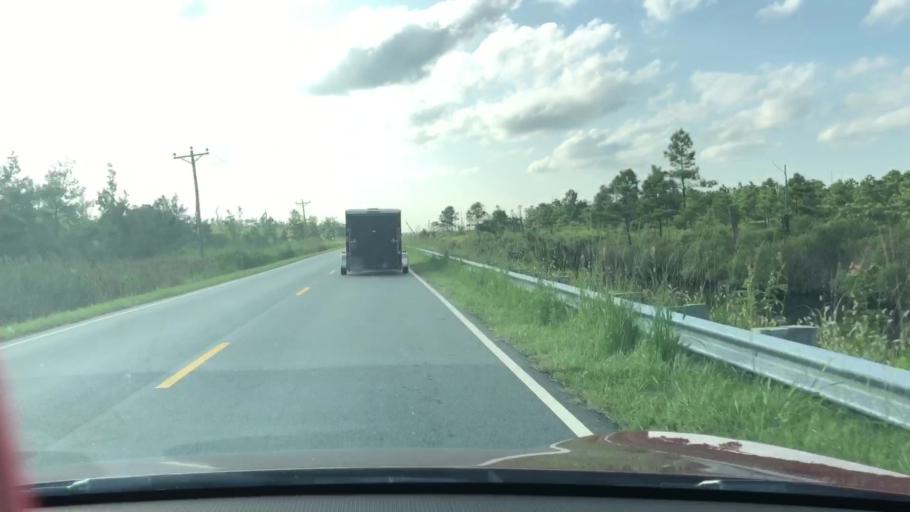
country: US
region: North Carolina
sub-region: Dare County
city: Wanchese
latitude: 35.6185
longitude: -75.8353
